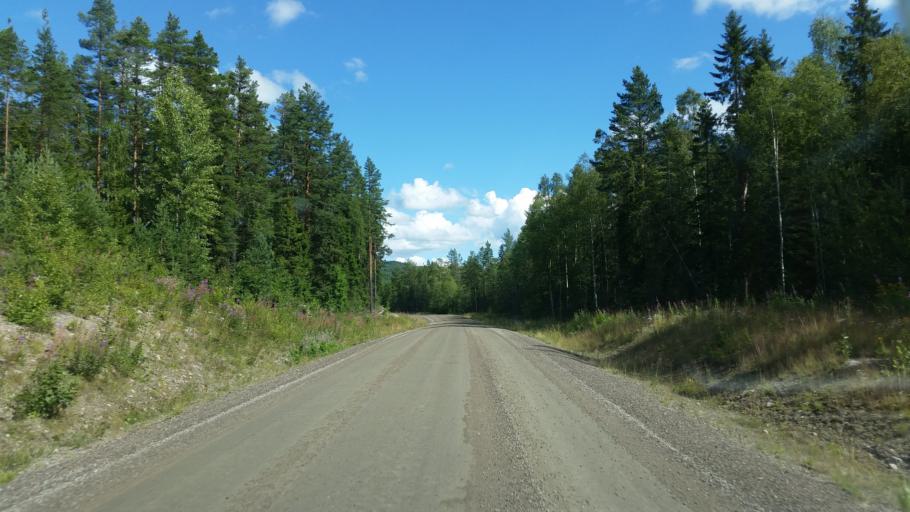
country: SE
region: Gaevleborg
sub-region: Ljusdals Kommun
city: Ljusdal
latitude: 61.9416
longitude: 16.1811
